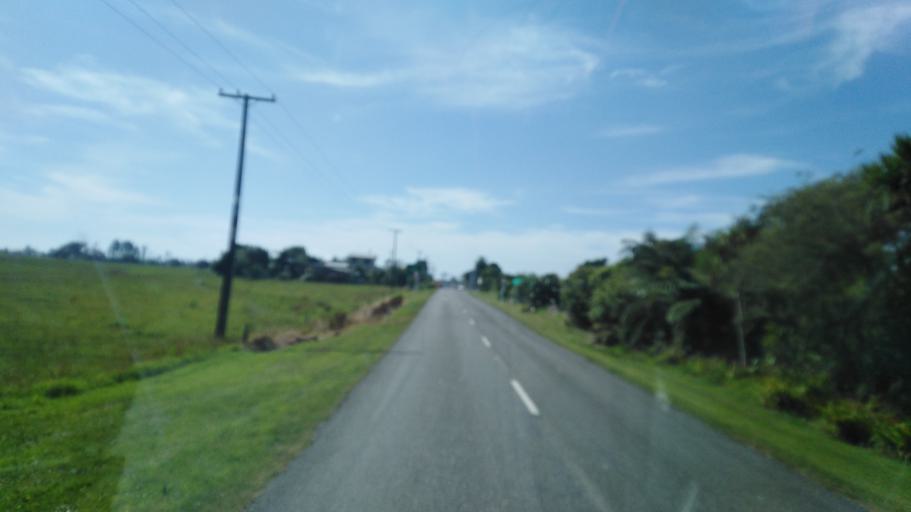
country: NZ
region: West Coast
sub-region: Buller District
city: Westport
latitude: -41.2541
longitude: 172.1299
